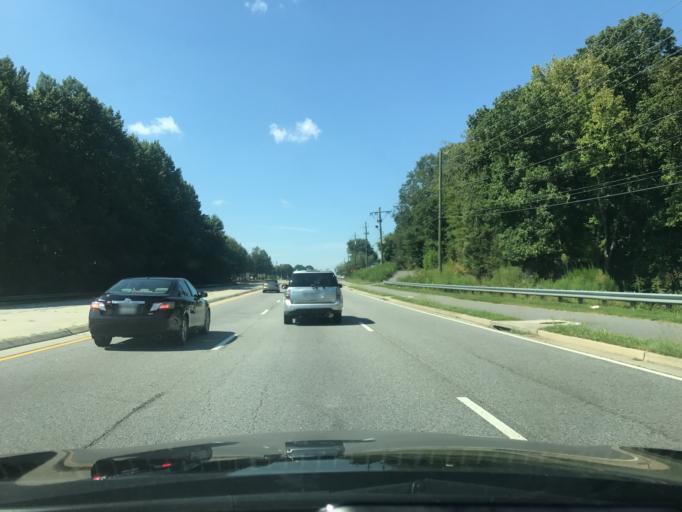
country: US
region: Georgia
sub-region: Gwinnett County
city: Duluth
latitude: 34.0185
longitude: -84.1620
